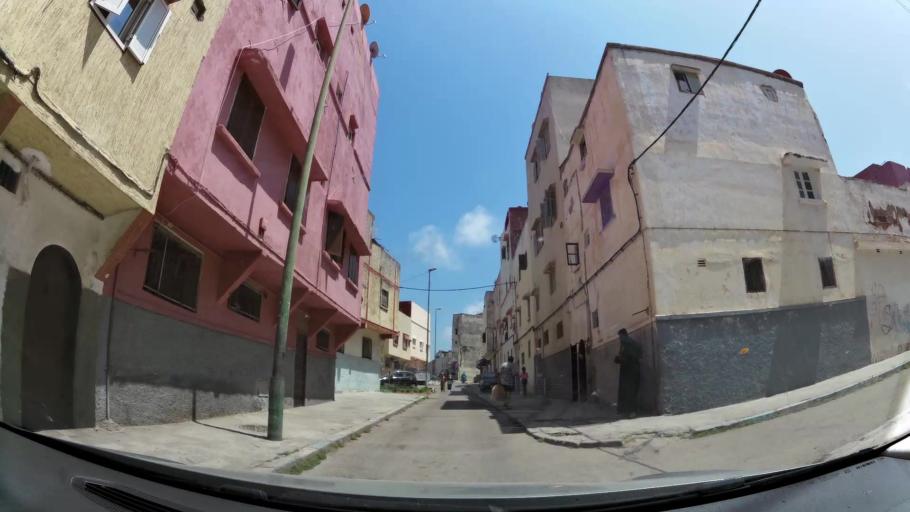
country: MA
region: Rabat-Sale-Zemmour-Zaer
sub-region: Rabat
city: Rabat
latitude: 34.0107
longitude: -6.8639
